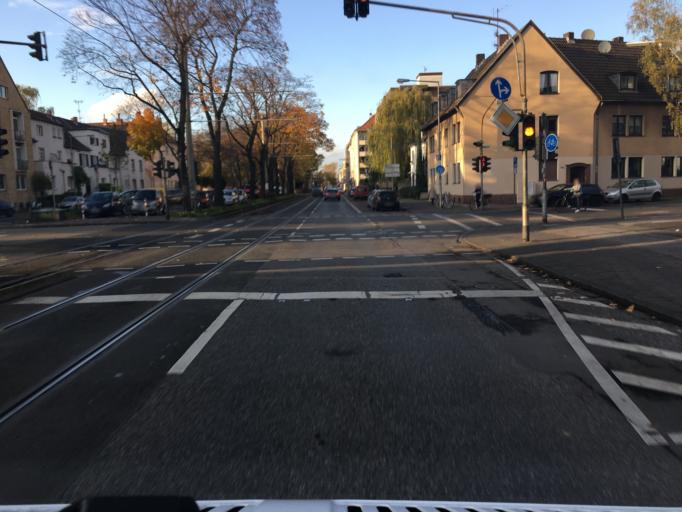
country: DE
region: North Rhine-Westphalia
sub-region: Regierungsbezirk Koln
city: Neustadt/Sued
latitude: 50.9215
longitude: 6.9144
